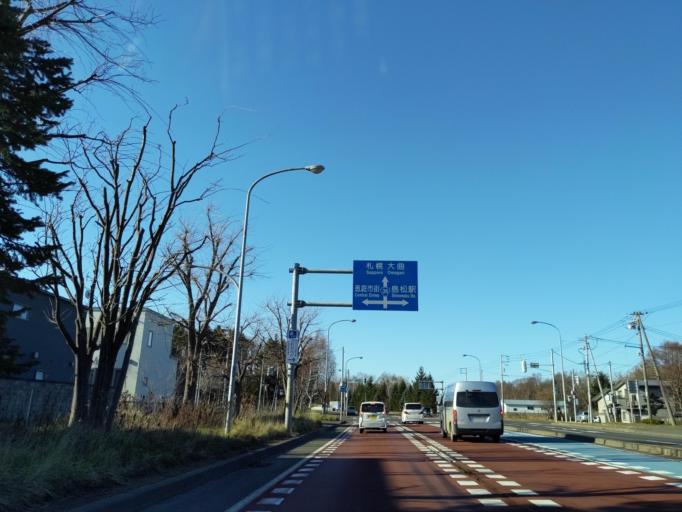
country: JP
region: Hokkaido
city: Kitahiroshima
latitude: 42.9053
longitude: 141.5613
